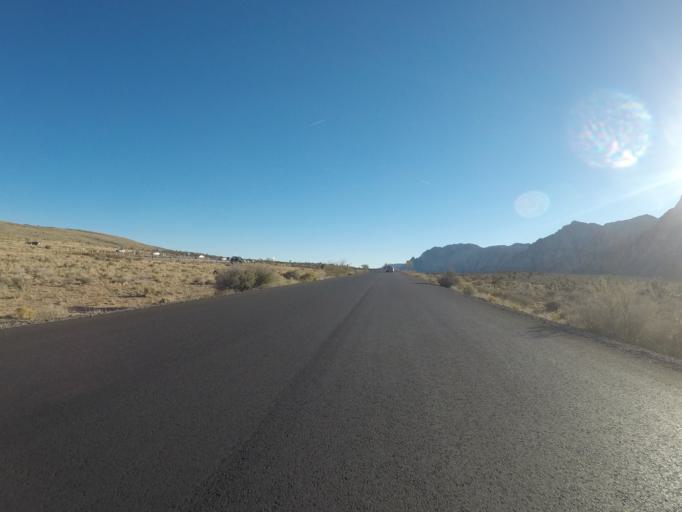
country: US
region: Nevada
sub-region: Clark County
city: Summerlin South
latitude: 36.1130
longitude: -115.4503
